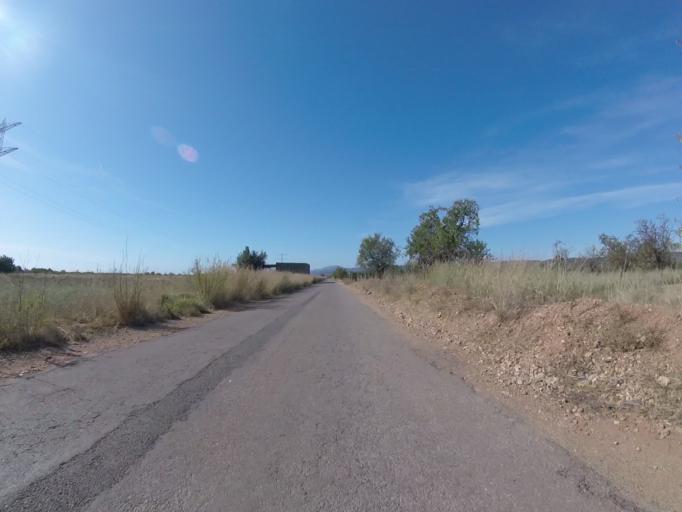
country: ES
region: Valencia
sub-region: Provincia de Castello
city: Torreblanca
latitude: 40.2155
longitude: 0.2171
